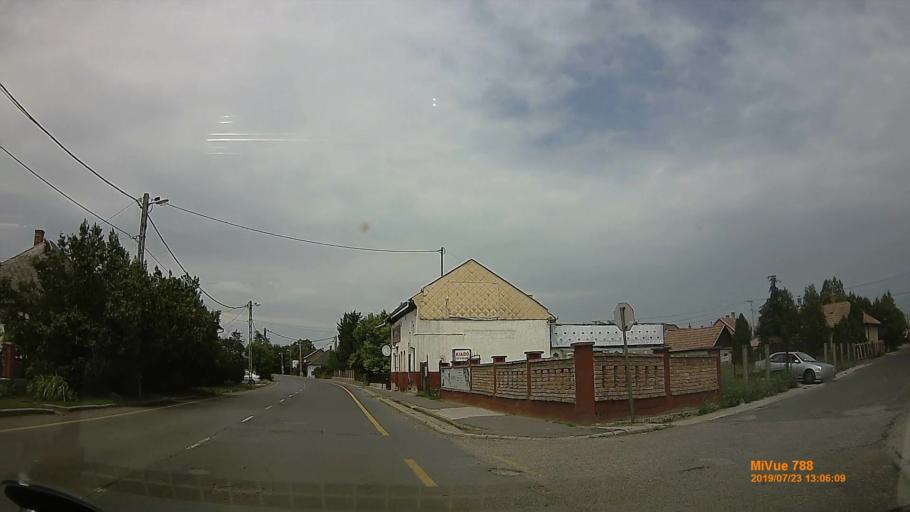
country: HU
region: Szabolcs-Szatmar-Bereg
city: Tiszavasvari
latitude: 47.9604
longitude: 21.3540
